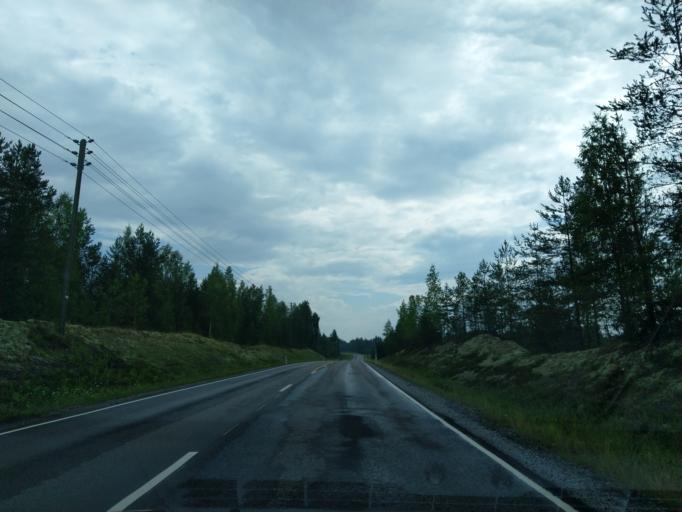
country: FI
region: South Karelia
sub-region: Imatra
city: Parikkala
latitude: 61.6410
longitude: 29.4266
